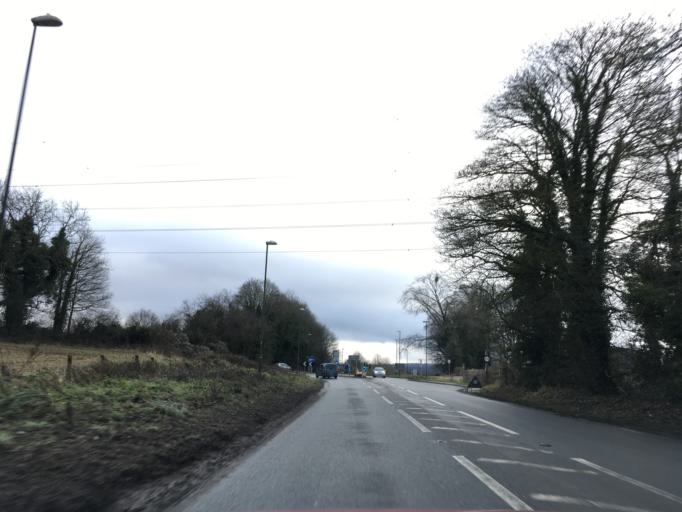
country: GB
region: England
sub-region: Gloucestershire
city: Charlton Kings
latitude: 51.8537
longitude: -2.0474
